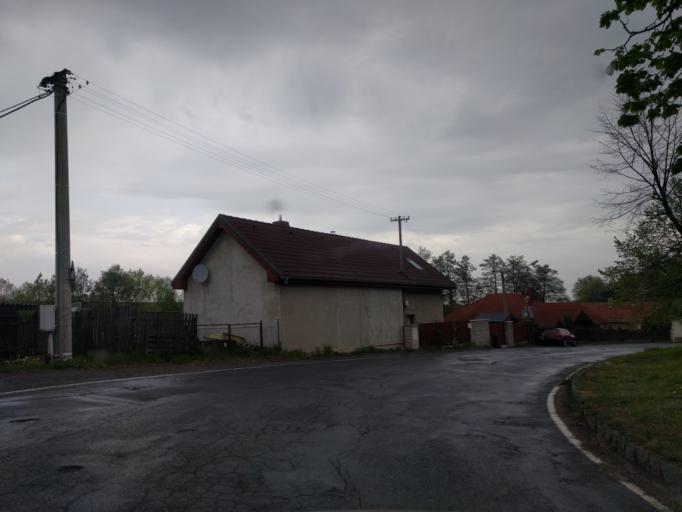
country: CZ
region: Central Bohemia
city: Dobris
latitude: 49.7060
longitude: 14.1449
